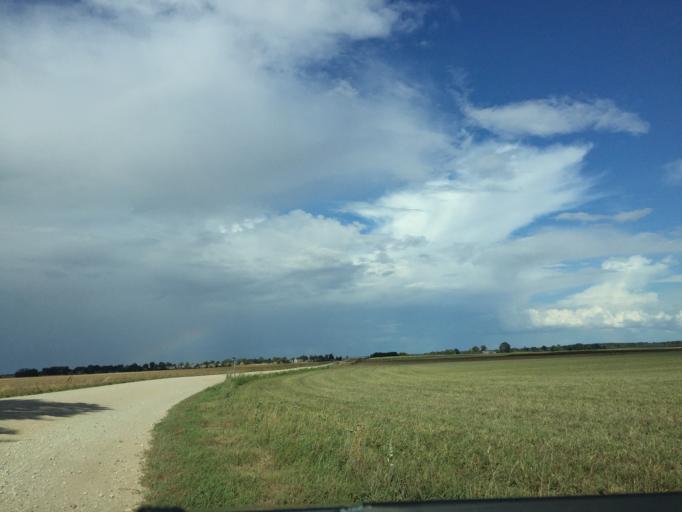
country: LV
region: Tervete
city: Zelmeni
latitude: 56.3112
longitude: 23.4308
